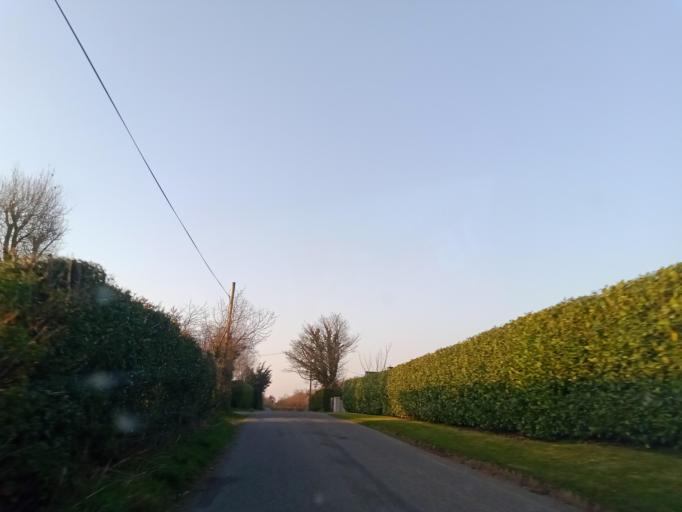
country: IE
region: Leinster
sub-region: Kilkenny
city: Kilkenny
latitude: 52.7268
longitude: -7.2367
